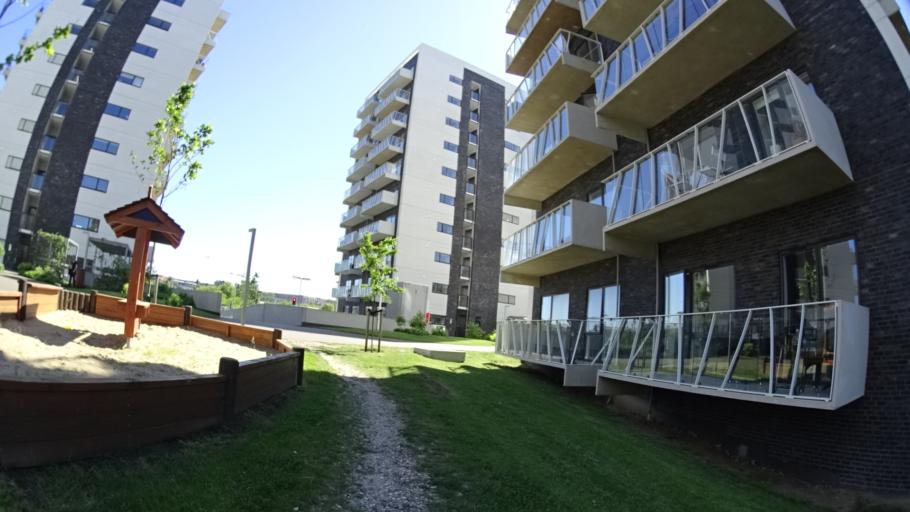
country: DK
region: Central Jutland
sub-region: Arhus Kommune
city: Arhus
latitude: 56.1530
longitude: 10.1887
